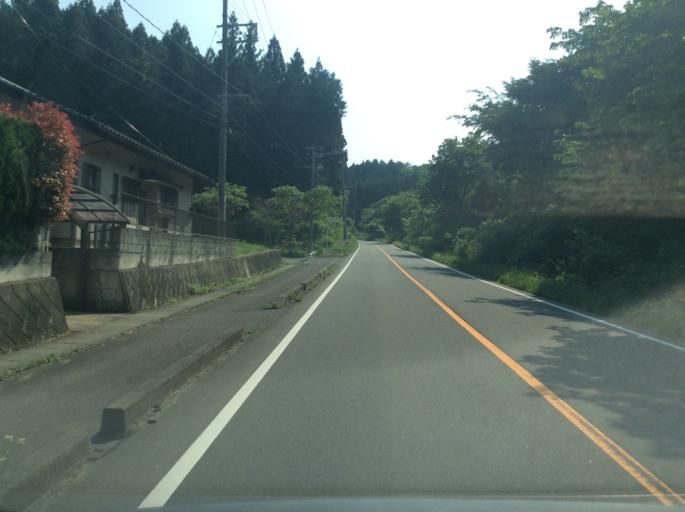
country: JP
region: Tochigi
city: Kuroiso
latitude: 37.0920
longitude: 140.2247
